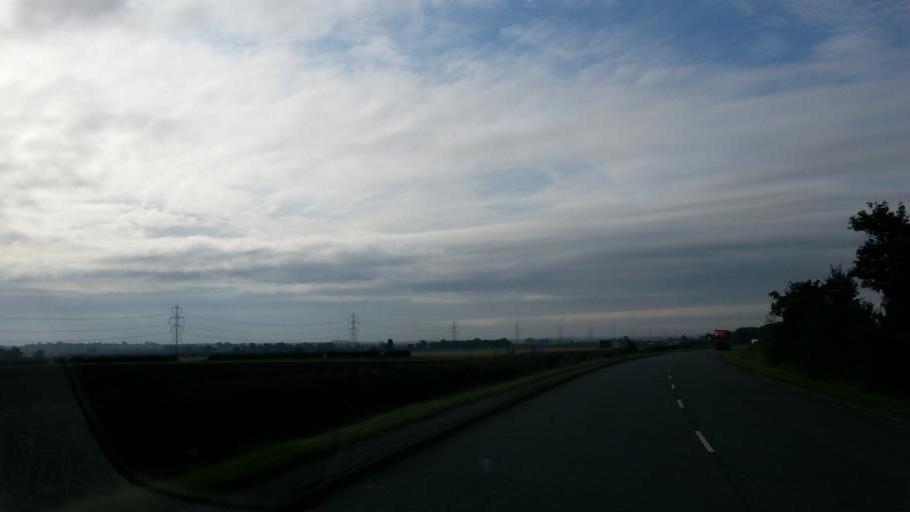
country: GB
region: England
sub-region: Lincolnshire
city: Long Bennington
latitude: 53.0344
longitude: -0.7691
